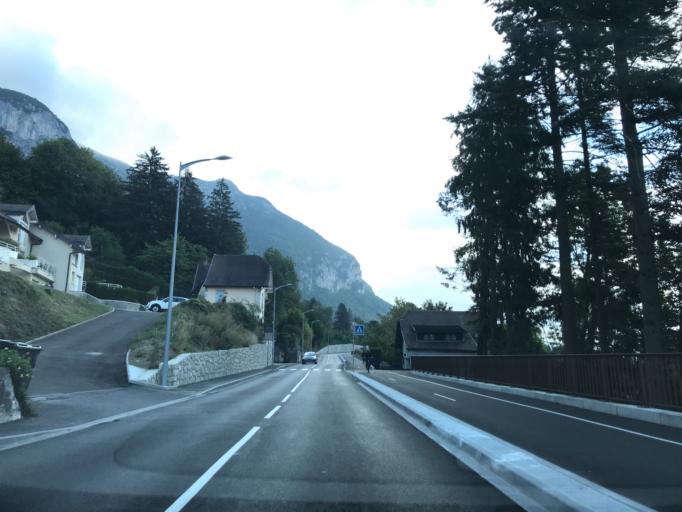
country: FR
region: Rhone-Alpes
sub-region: Departement de la Haute-Savoie
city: Veyrier-du-Lac
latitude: 45.8910
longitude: 6.1712
